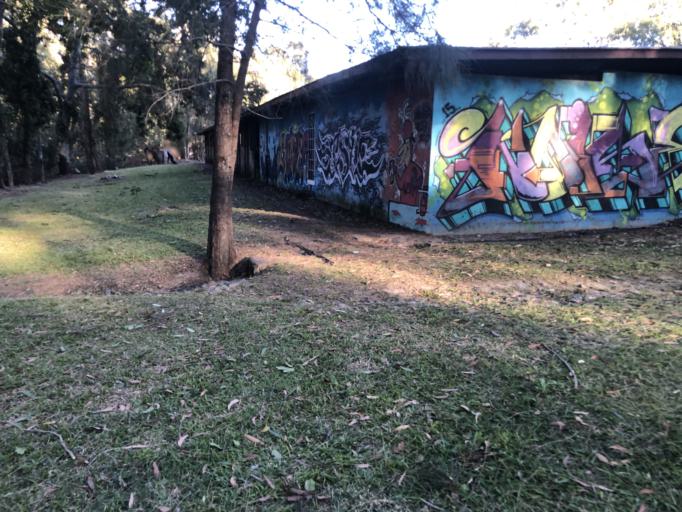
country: AU
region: New South Wales
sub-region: Coffs Harbour
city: Coffs Harbour
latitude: -30.2943
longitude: 153.1209
